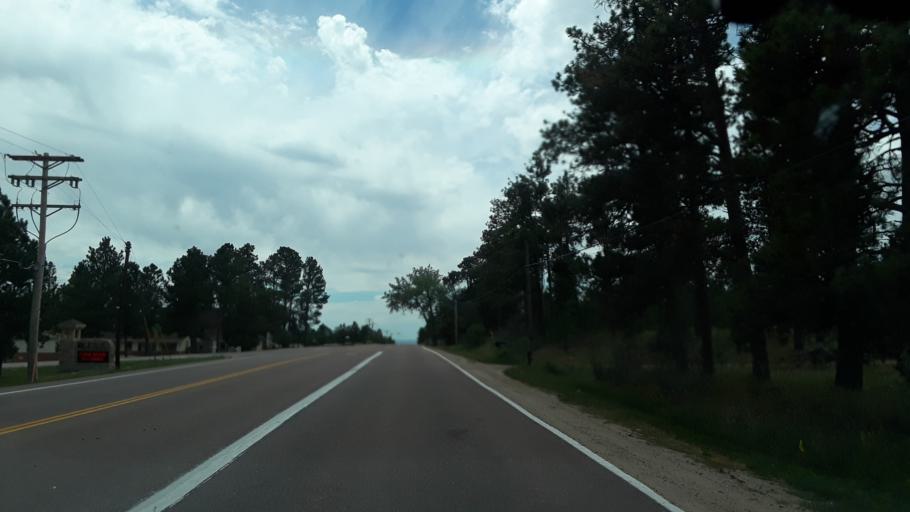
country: US
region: Colorado
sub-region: El Paso County
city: Black Forest
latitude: 38.9907
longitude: -104.7004
